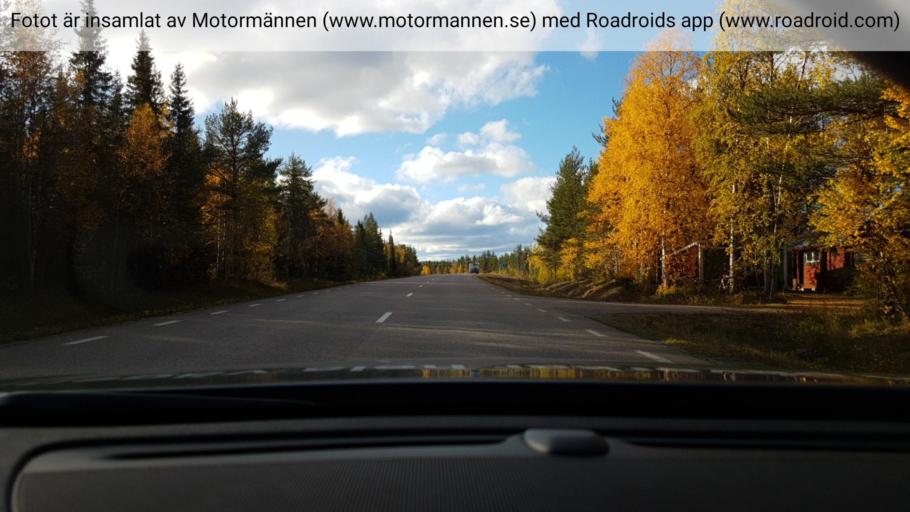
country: SE
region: Norrbotten
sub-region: Gallivare Kommun
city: Gaellivare
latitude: 67.1333
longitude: 20.5842
